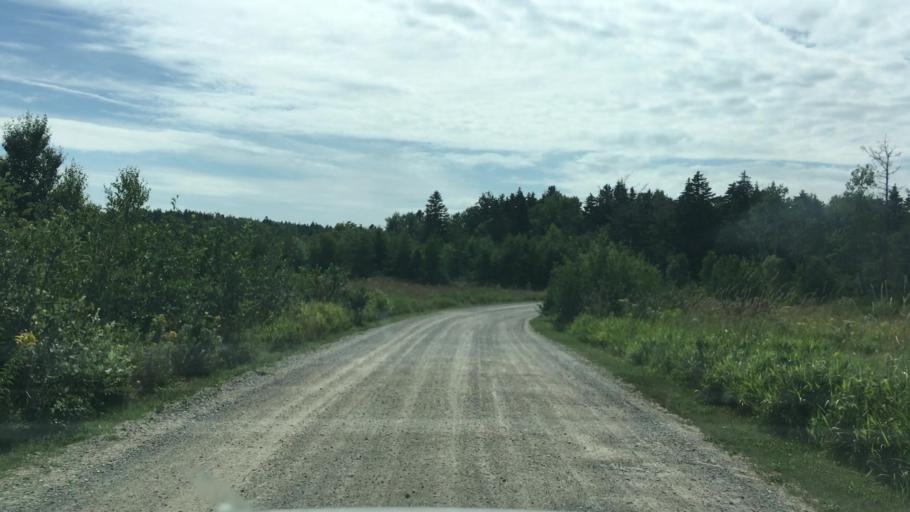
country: US
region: Maine
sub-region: Washington County
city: Eastport
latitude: 44.9065
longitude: -67.0115
